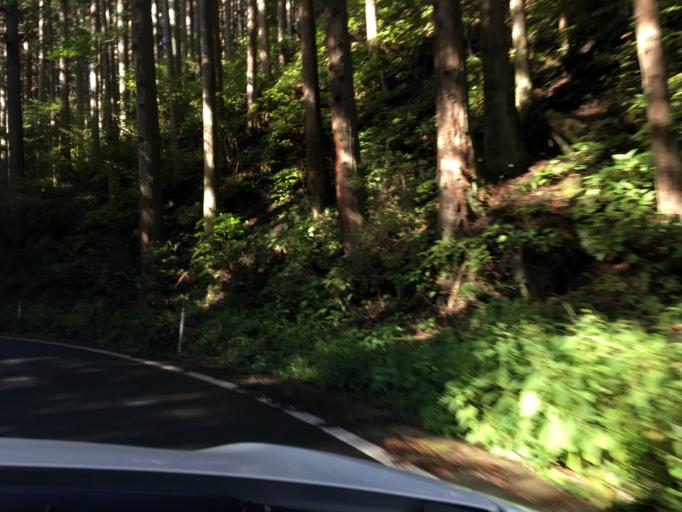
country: JP
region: Fukushima
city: Ishikawa
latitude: 37.1234
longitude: 140.5589
